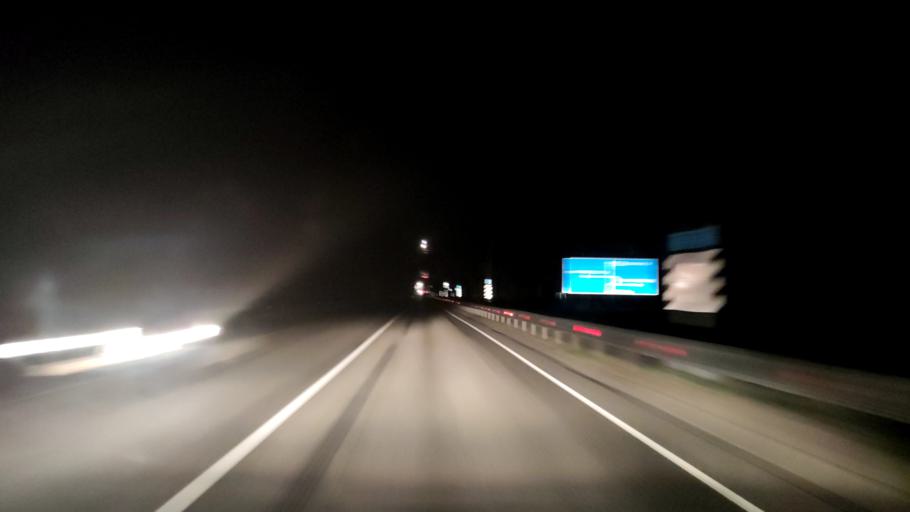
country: RU
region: Voronezj
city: Nizhnedevitsk
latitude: 51.5648
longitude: 38.3604
